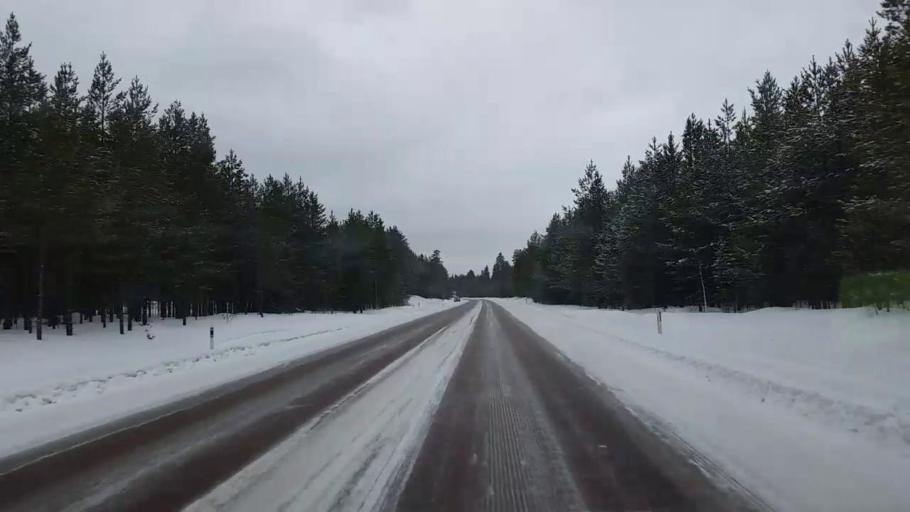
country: SE
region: Jaemtland
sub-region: Bergs Kommun
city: Hoverberg
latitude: 62.4538
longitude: 14.5534
